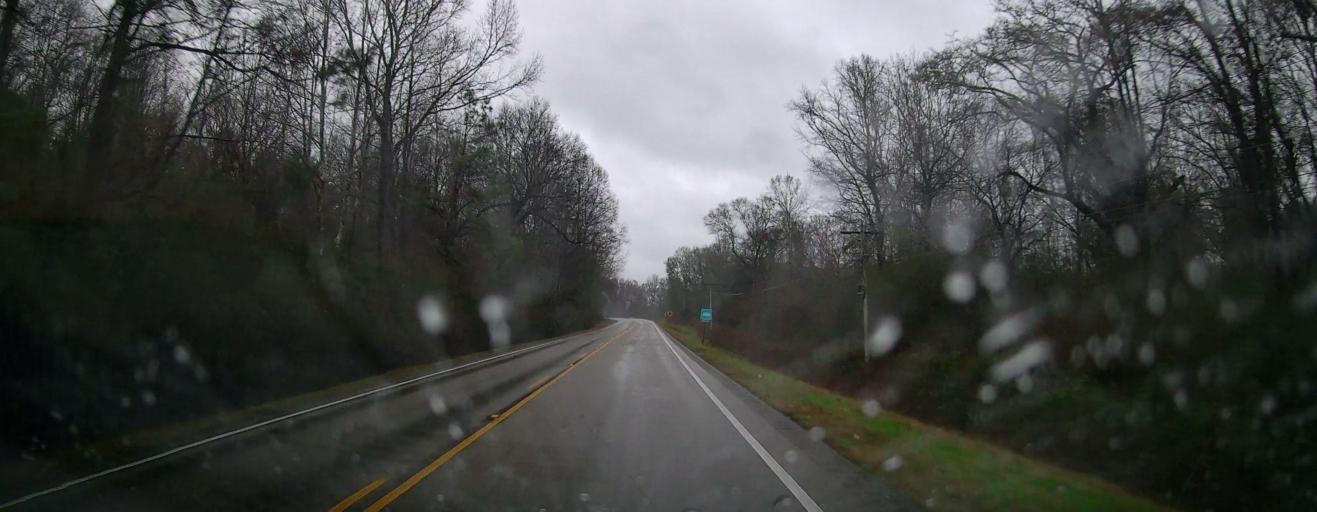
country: US
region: Alabama
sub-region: Autauga County
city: Prattville
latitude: 32.5087
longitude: -86.5871
